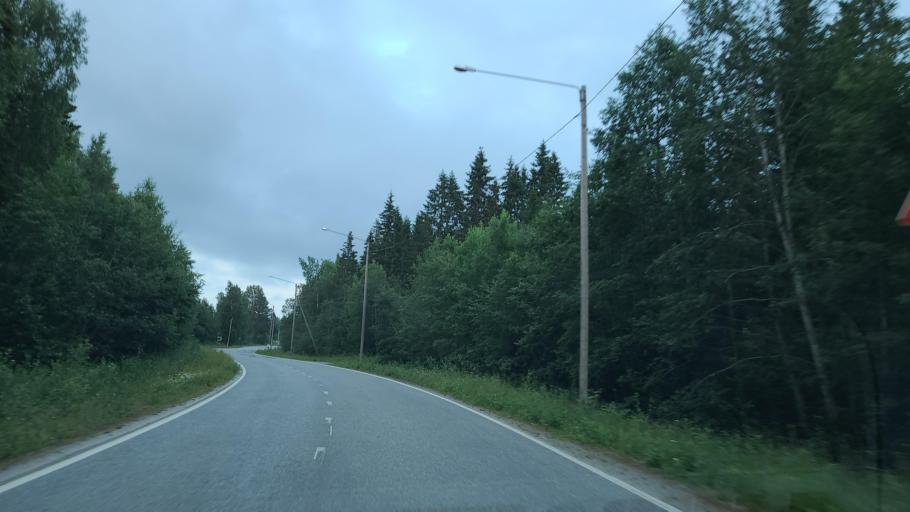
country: FI
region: Ostrobothnia
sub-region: Vaasa
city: Replot
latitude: 63.2859
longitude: 21.1185
